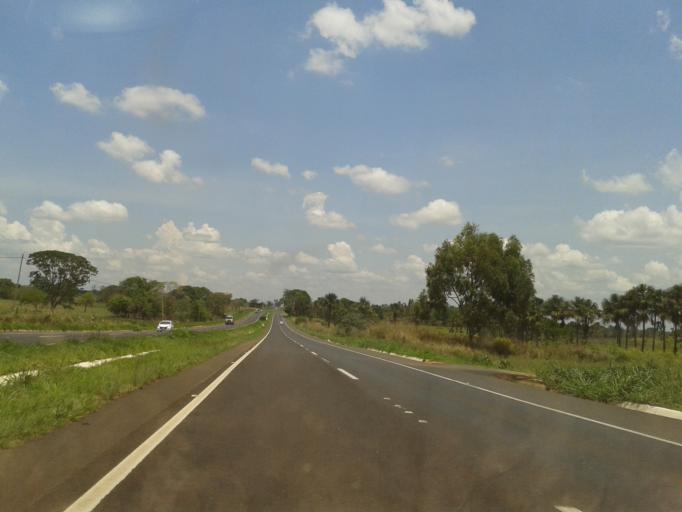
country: BR
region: Minas Gerais
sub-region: Monte Alegre De Minas
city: Monte Alegre de Minas
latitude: -18.8754
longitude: -48.6019
